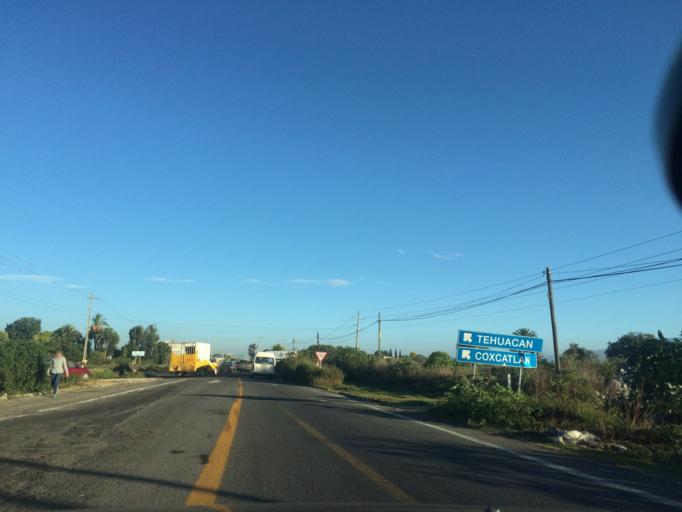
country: MX
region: Puebla
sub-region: Santiago Miahuatlan
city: San Jose Monte Chiquito
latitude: 18.4877
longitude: -97.4572
